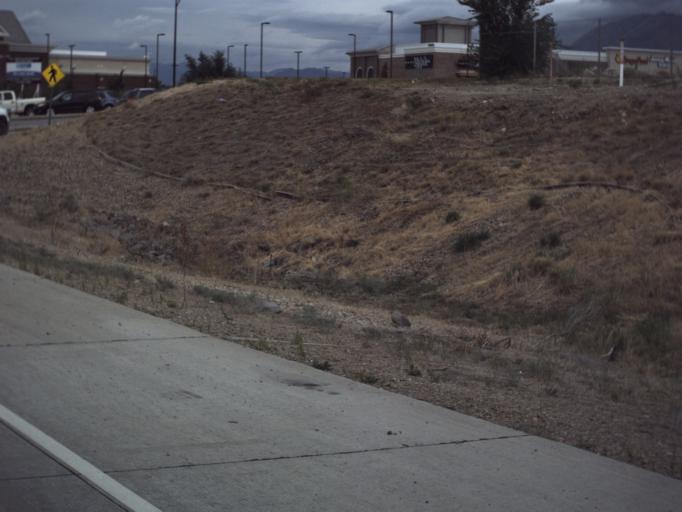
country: US
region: Utah
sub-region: Salt Lake County
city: Draper
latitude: 40.5436
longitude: -111.8938
